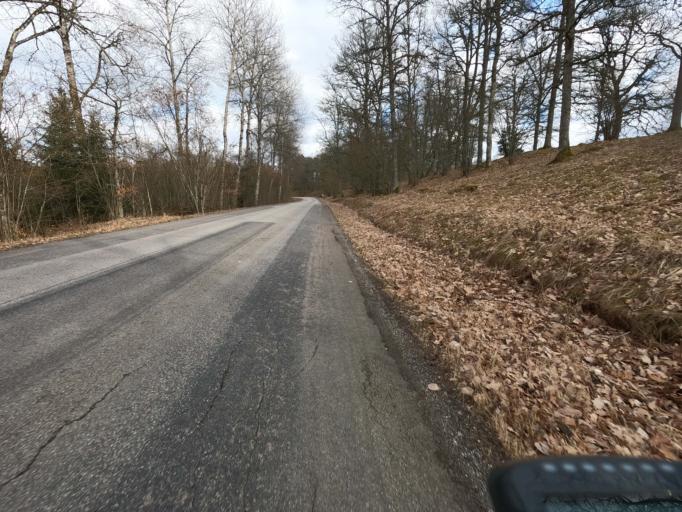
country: SE
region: Kronoberg
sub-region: Alvesta Kommun
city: Vislanda
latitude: 56.8215
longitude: 14.5172
